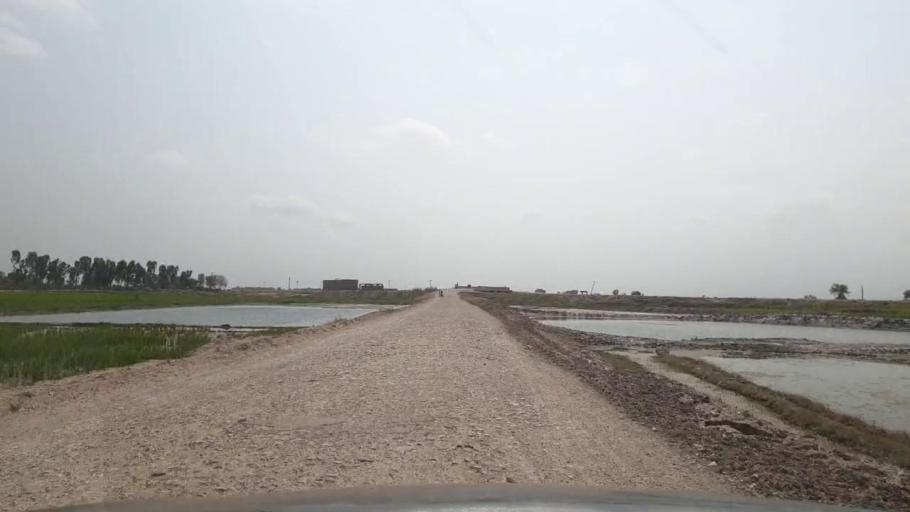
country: PK
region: Sindh
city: Ratodero
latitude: 27.8392
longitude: 68.3334
